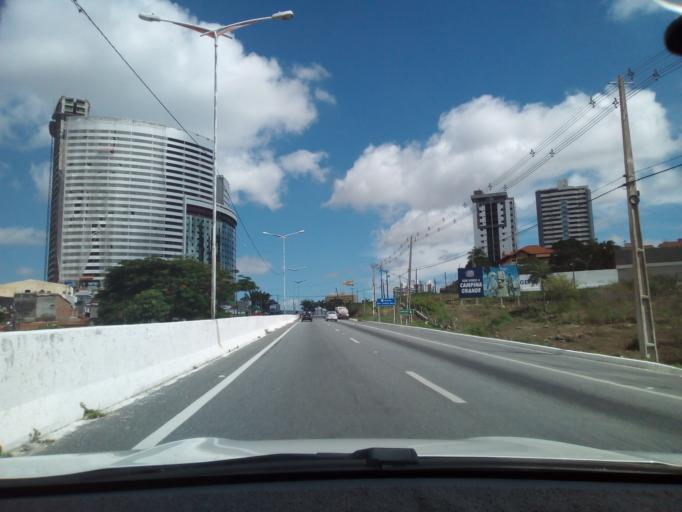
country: BR
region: Paraiba
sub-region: Campina Grande
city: Campina Grande
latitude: -7.2386
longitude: -35.8645
